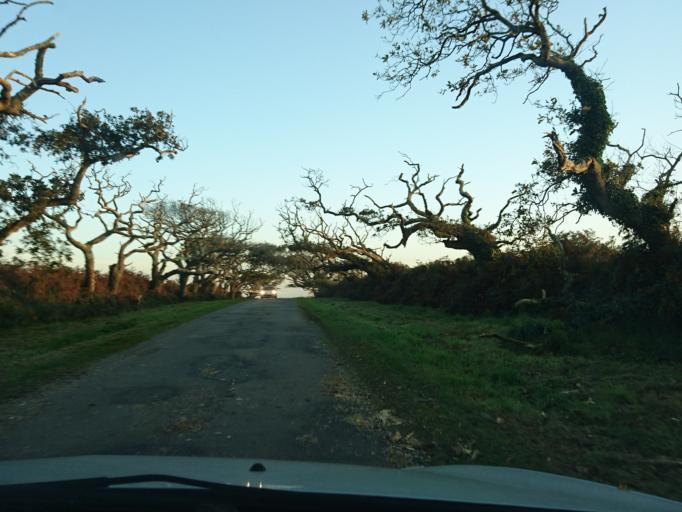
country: FR
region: Brittany
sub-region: Departement du Finistere
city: Lanrivoare
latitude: 48.4741
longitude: -4.6655
